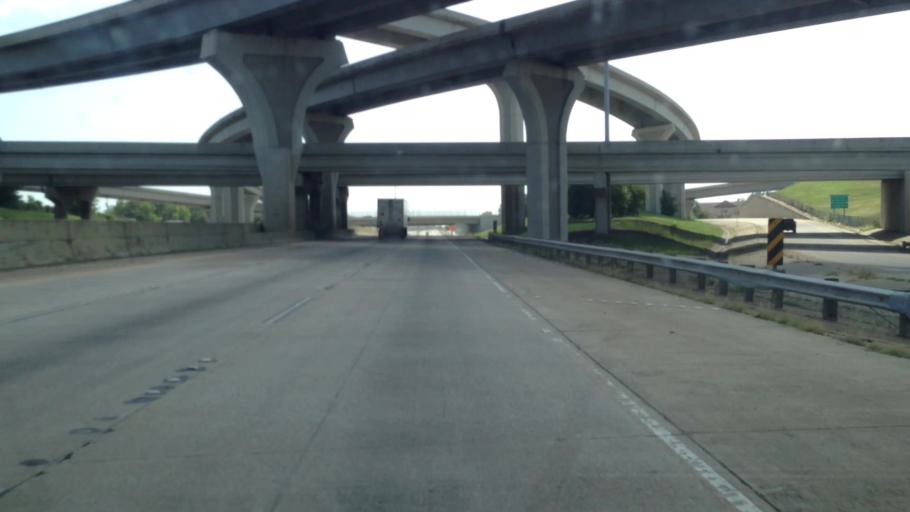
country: US
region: Louisiana
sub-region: Caddo Parish
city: Shreveport
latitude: 32.4972
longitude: -93.7586
